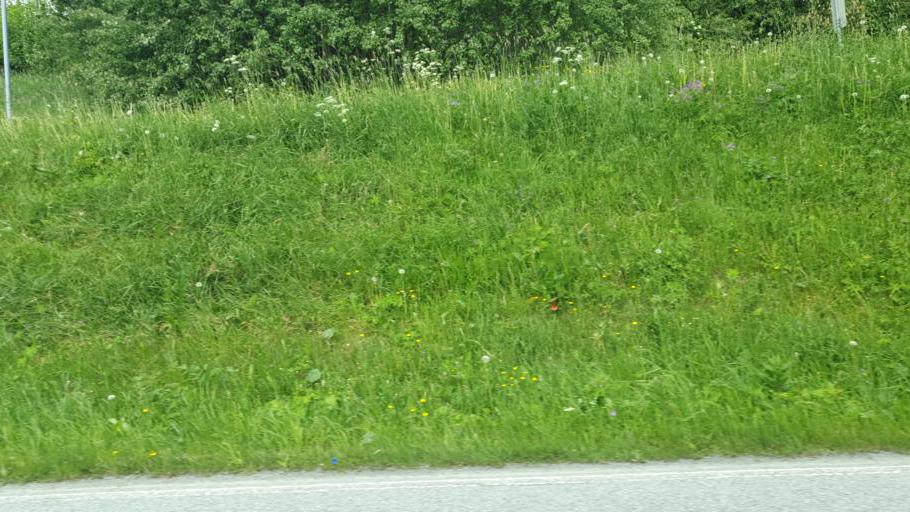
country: NO
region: Sor-Trondelag
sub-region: Trondheim
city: Trondheim
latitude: 63.5552
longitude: 10.2255
